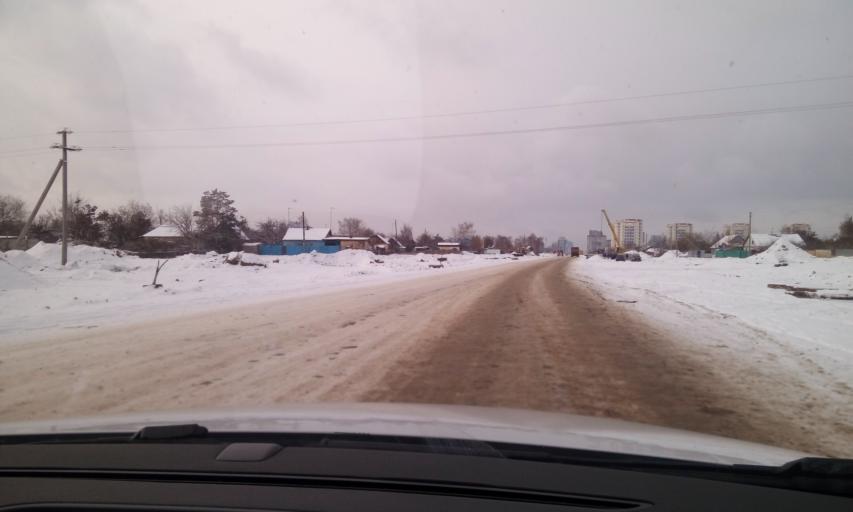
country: KZ
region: Astana Qalasy
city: Astana
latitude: 51.1174
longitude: 71.5153
